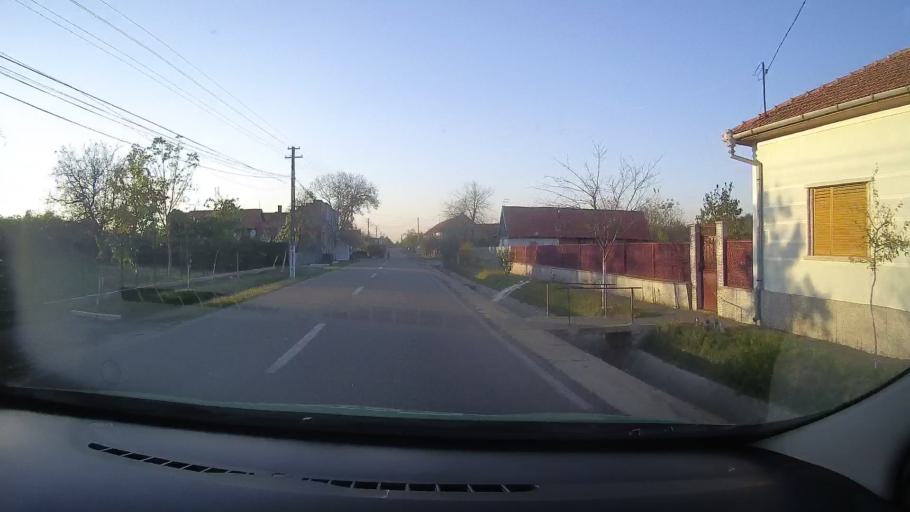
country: RO
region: Timis
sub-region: Comuna Traian Vuia
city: Traian Vuia
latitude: 45.7951
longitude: 22.0691
